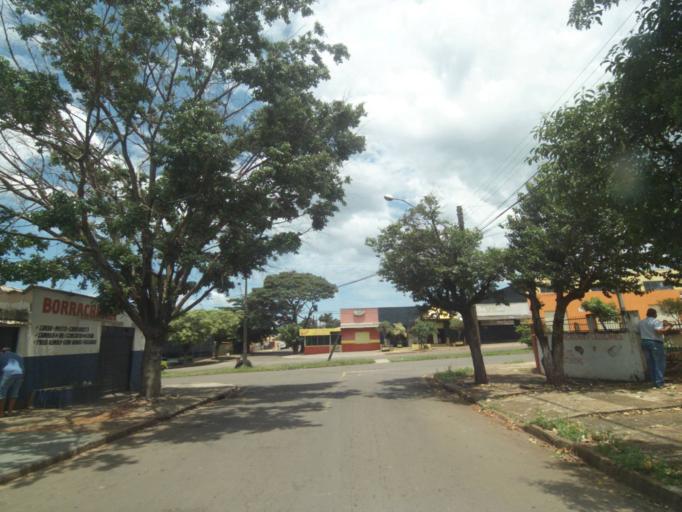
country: BR
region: Parana
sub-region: Londrina
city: Londrina
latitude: -23.3112
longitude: -51.2161
